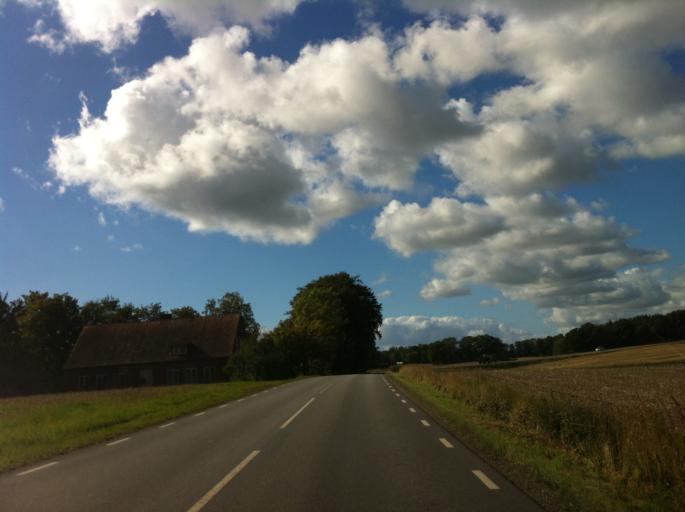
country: SE
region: Skane
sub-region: Tomelilla Kommun
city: Tomelilla
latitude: 55.6505
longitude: 13.9577
